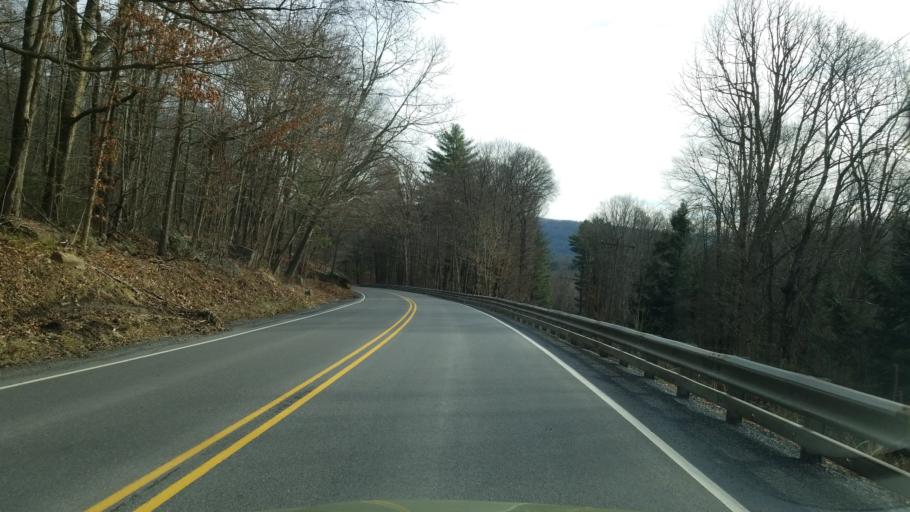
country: US
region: Pennsylvania
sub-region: Indiana County
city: Johnsonburg
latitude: 40.8868
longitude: -78.7727
